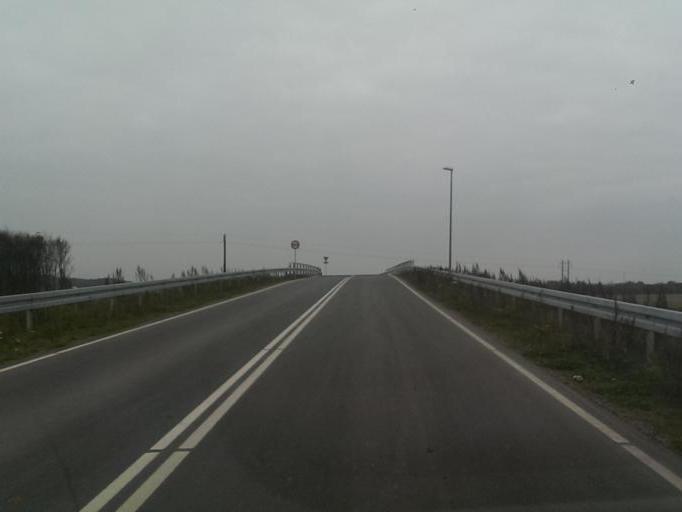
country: DK
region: South Denmark
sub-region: Esbjerg Kommune
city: Tjaereborg
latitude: 55.4704
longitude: 8.5582
